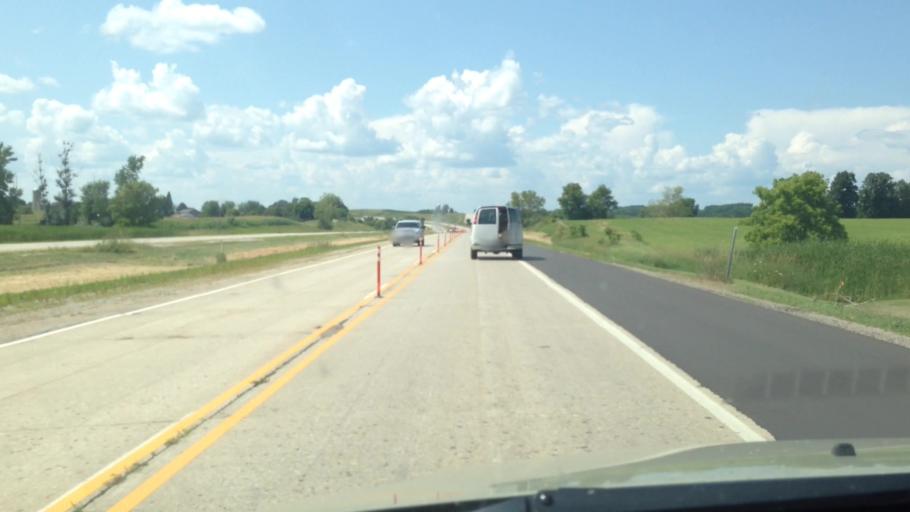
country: US
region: Wisconsin
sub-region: Shawano County
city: Bonduel
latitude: 44.7131
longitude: -88.3866
